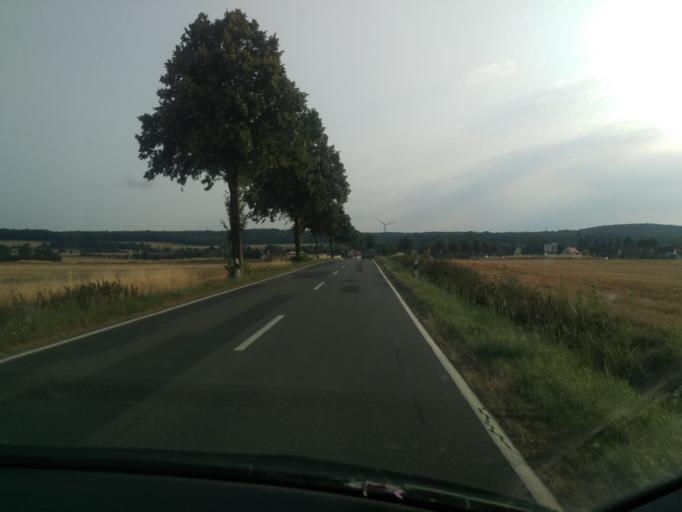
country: DE
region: Lower Saxony
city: Schellerten
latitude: 52.1396
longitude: 10.0728
